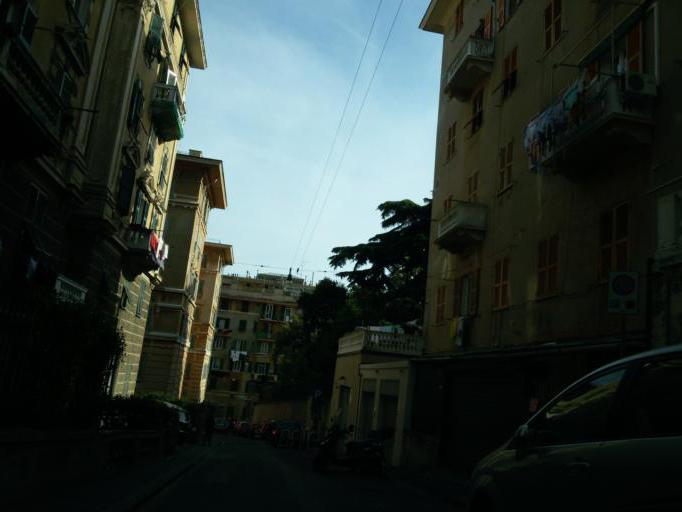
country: IT
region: Liguria
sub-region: Provincia di Genova
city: Genoa
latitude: 44.4086
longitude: 8.9632
